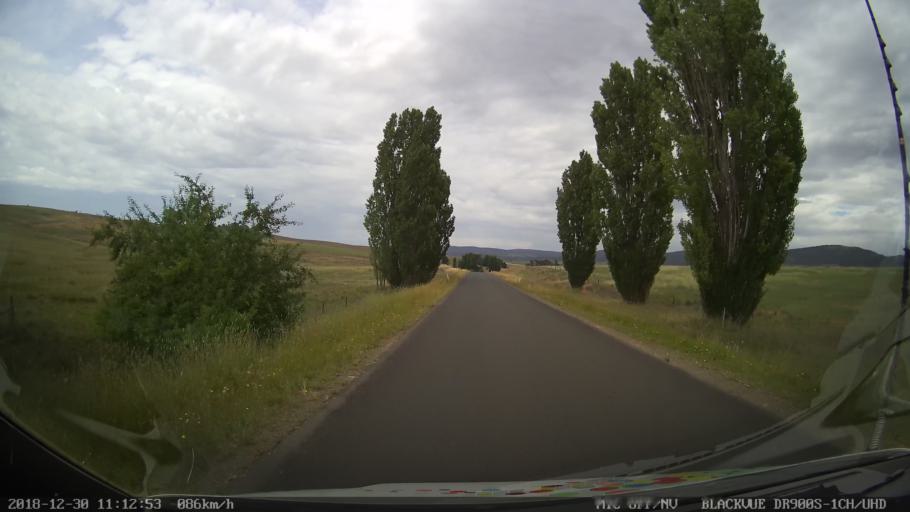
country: AU
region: New South Wales
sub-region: Snowy River
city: Jindabyne
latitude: -36.5310
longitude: 148.7506
